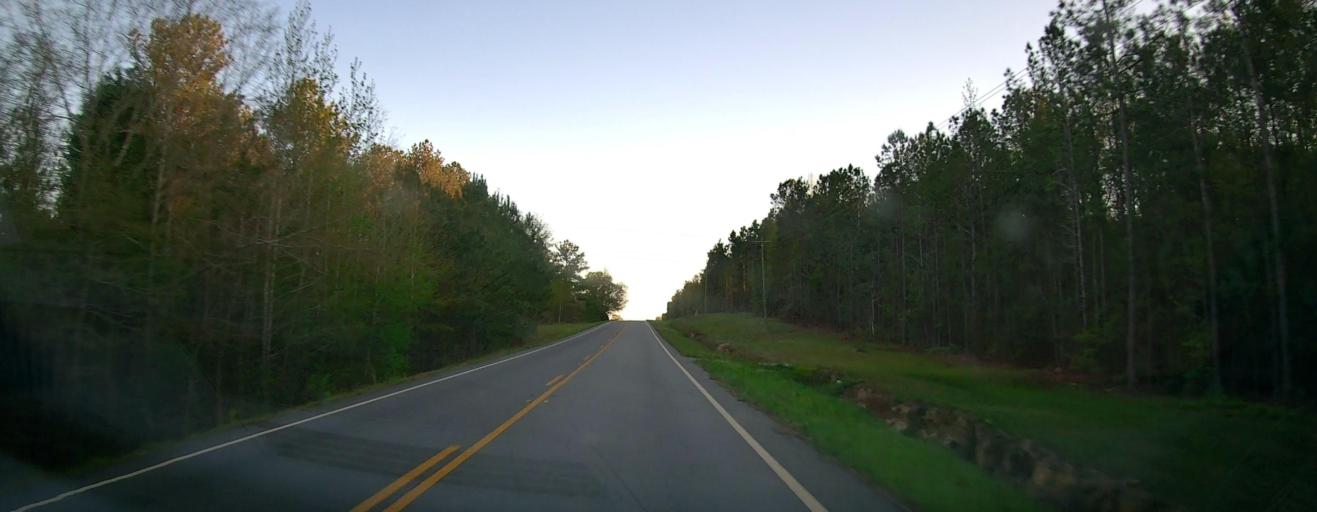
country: US
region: Georgia
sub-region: Talbot County
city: Talbotton
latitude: 32.5489
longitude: -84.5697
